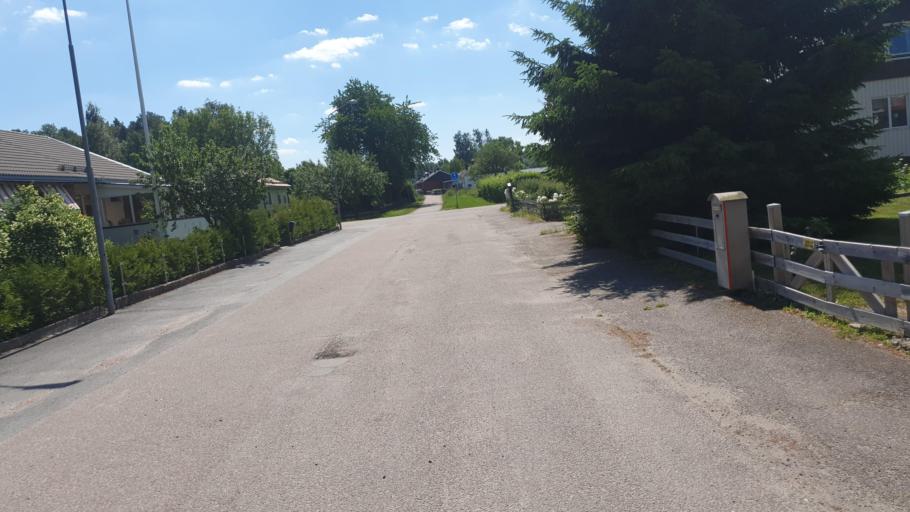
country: SE
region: Uppsala
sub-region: Osthammars Kommun
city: Gimo
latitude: 60.1713
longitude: 18.1772
